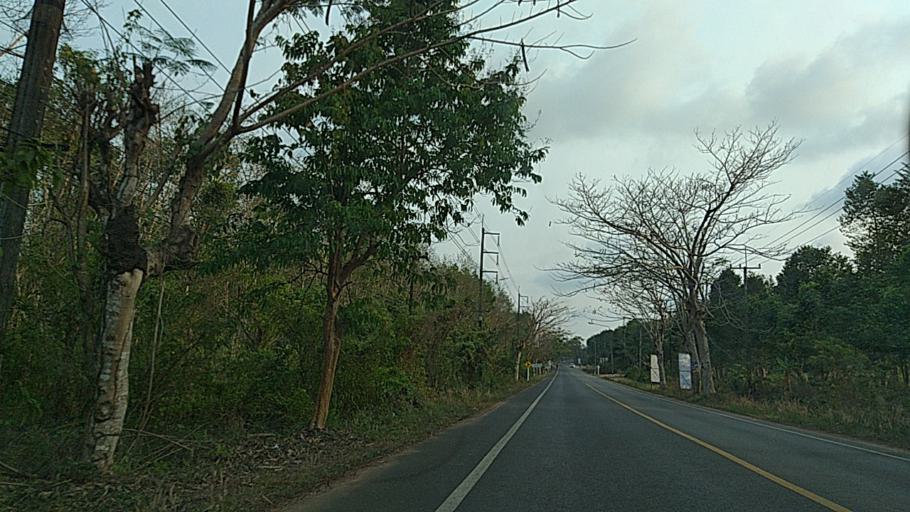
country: TH
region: Trat
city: Laem Ngop
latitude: 12.2744
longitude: 102.3056
